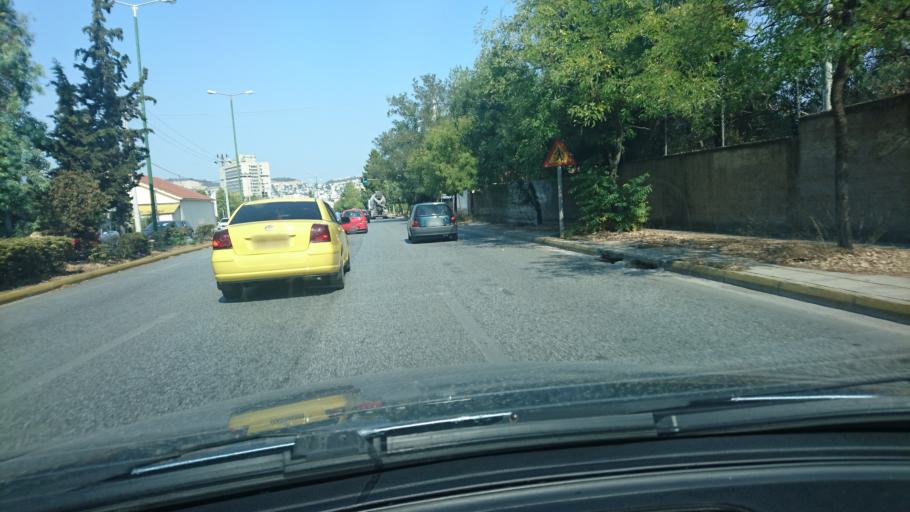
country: GR
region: Attica
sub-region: Nomarchia Athinas
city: Papagou
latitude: 37.9854
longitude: 23.7820
